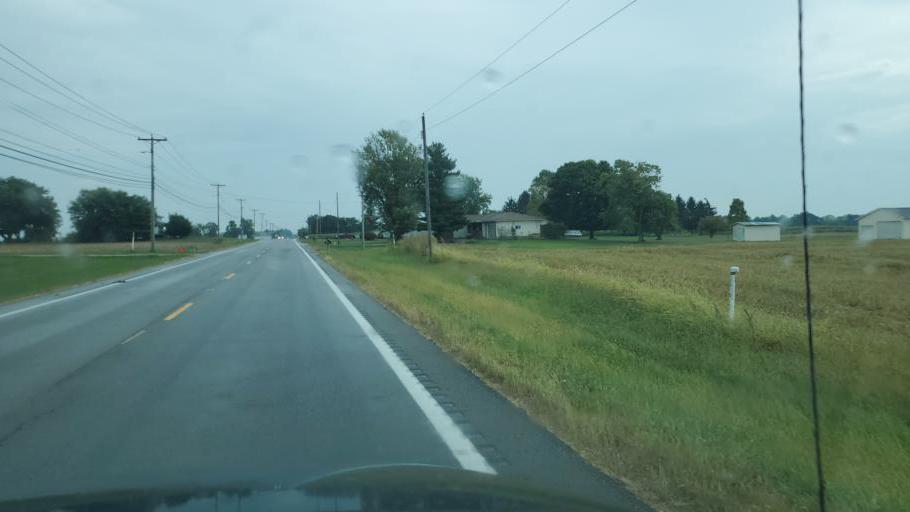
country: US
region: Ohio
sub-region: Licking County
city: Harbor Hills
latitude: 39.9607
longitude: -82.4507
